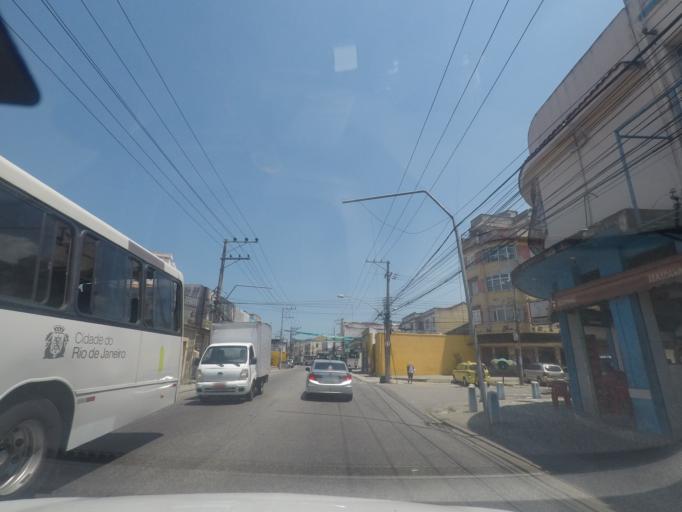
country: BR
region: Rio de Janeiro
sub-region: Duque De Caxias
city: Duque de Caxias
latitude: -22.8479
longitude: -43.2672
